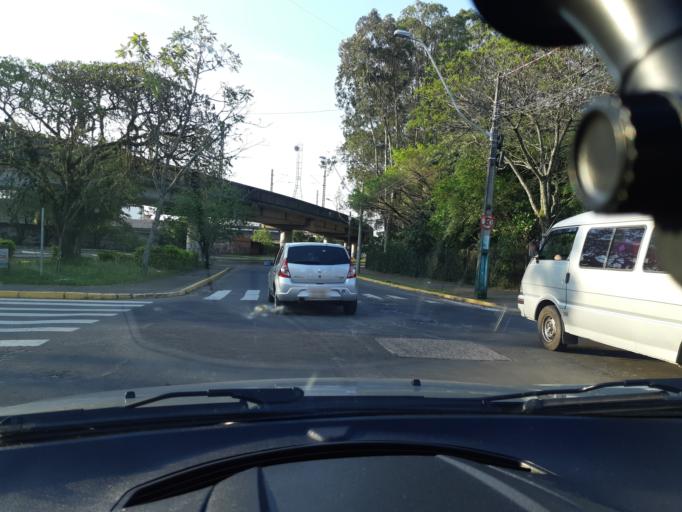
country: BR
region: Rio Grande do Sul
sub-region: Sao Leopoldo
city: Sao Leopoldo
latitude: -29.7676
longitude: -51.1398
